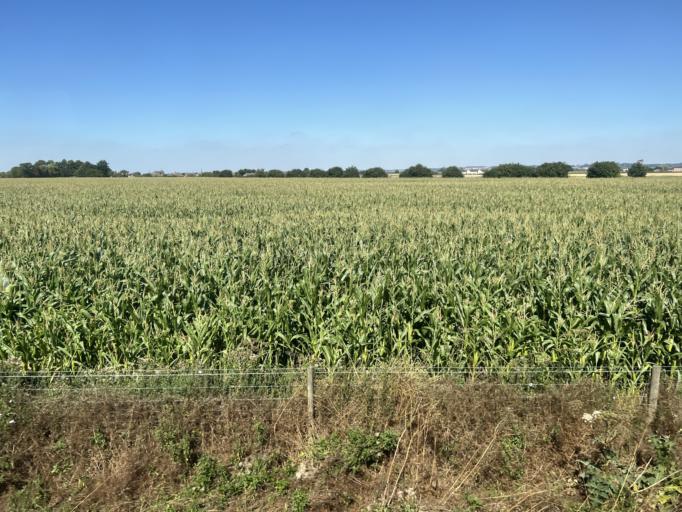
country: GB
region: England
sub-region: Lincolnshire
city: Spilsby
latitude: 53.0933
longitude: 0.1015
